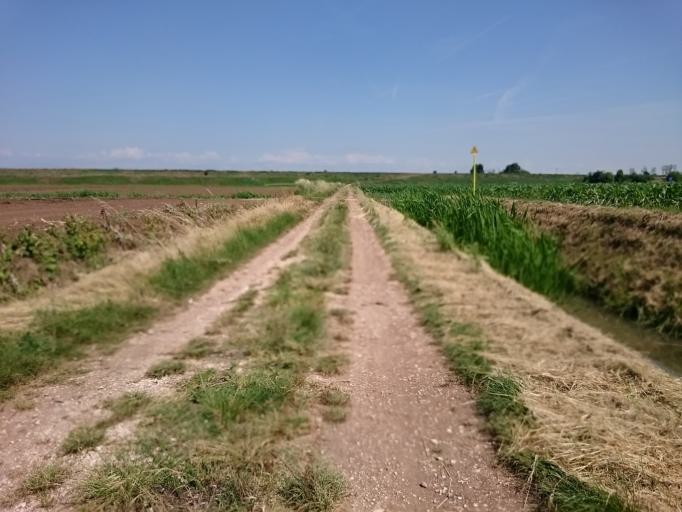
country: IT
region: Veneto
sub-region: Provincia di Padova
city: Saletto
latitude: 45.2560
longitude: 11.5621
